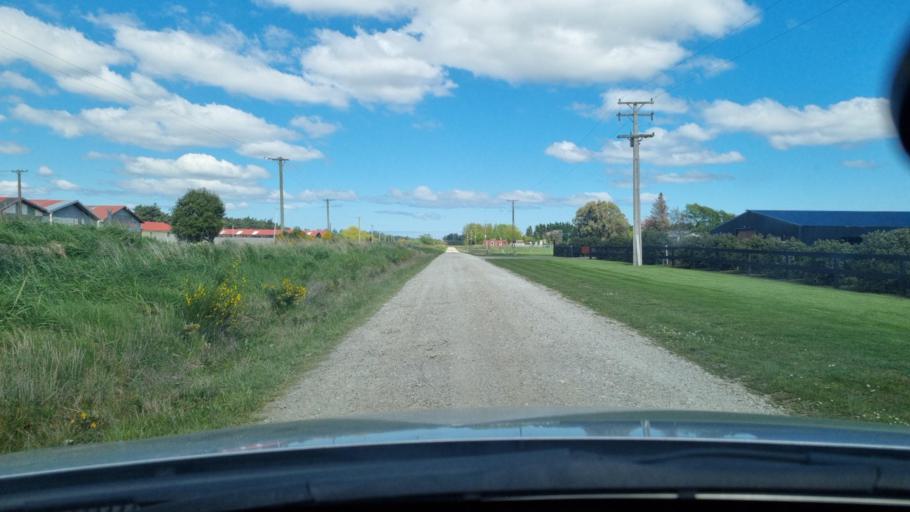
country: NZ
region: Southland
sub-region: Invercargill City
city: Invercargill
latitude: -46.3451
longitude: 168.3401
